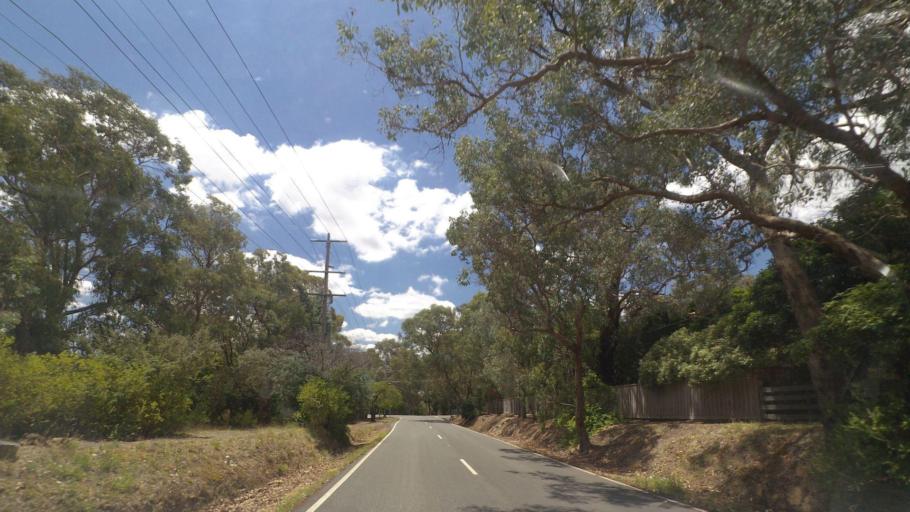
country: AU
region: Victoria
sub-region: Yarra Ranges
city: Chirnside Park
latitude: -37.7323
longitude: 145.2730
